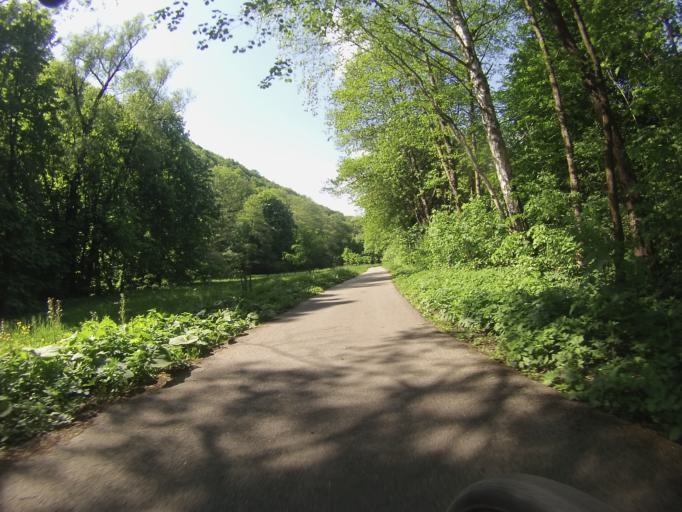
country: CZ
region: South Moravian
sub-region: Okres Blansko
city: Adamov
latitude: 49.3173
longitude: 16.6410
